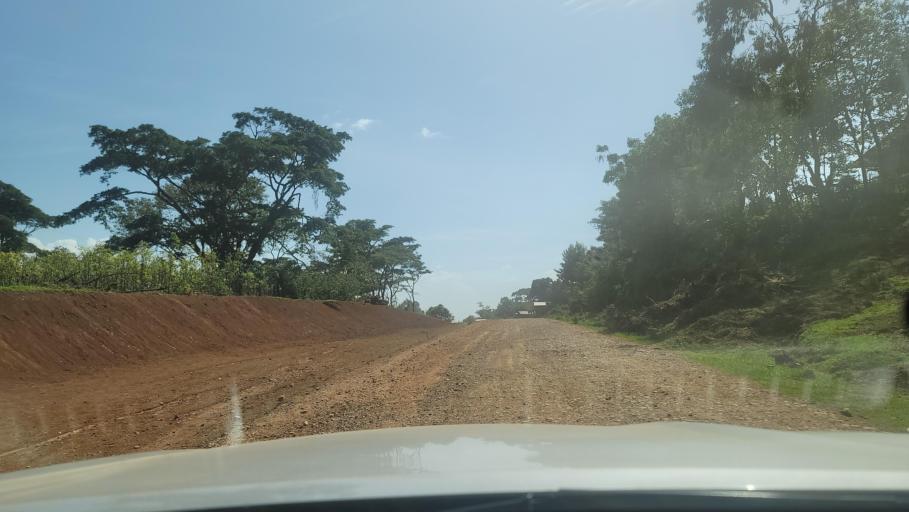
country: ET
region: Oromiya
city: Agaro
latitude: 7.8049
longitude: 36.4620
